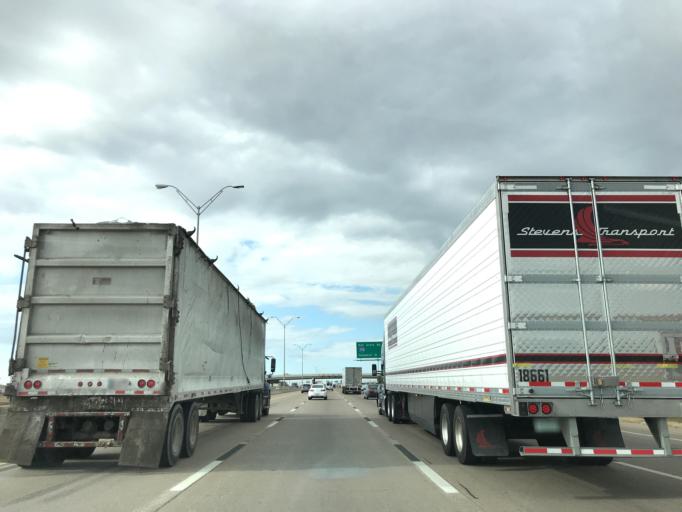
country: US
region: Texas
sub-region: Tarrant County
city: Forest Hill
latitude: 32.6637
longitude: -97.2898
